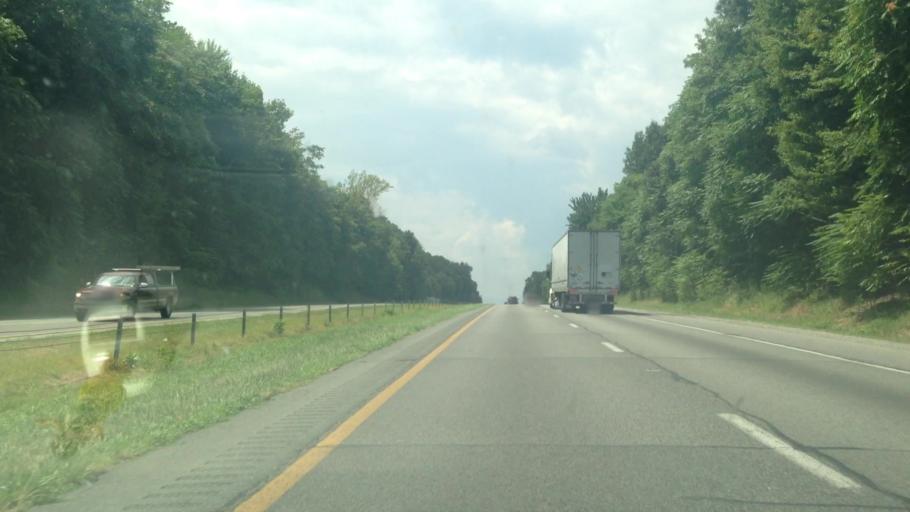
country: US
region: North Carolina
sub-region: Surry County
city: Pilot Mountain
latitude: 36.3481
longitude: -80.4649
